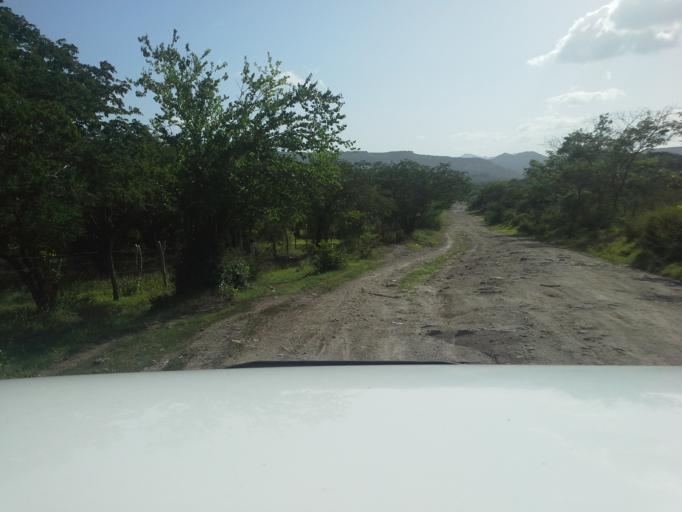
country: NI
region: Matagalpa
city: Ciudad Dario
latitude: 12.6598
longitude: -86.0731
